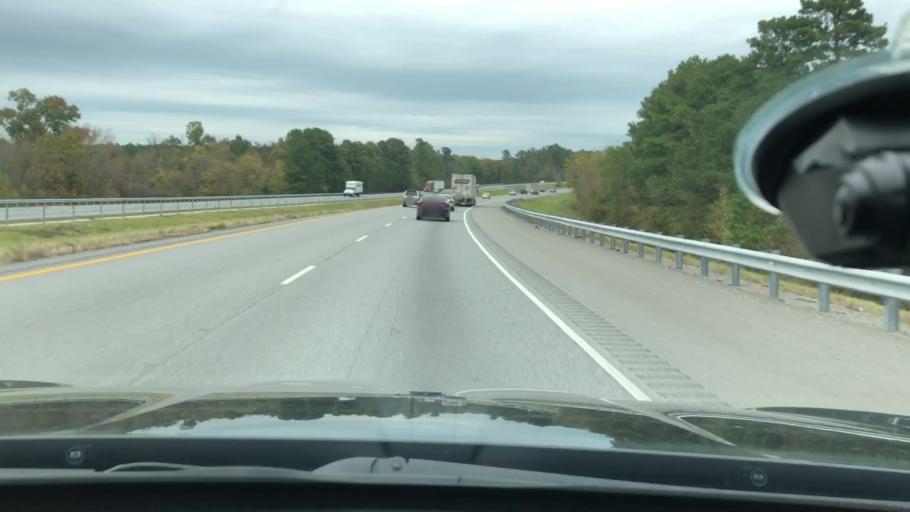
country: US
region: Arkansas
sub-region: Hempstead County
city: Hope
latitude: 33.6183
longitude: -93.7908
